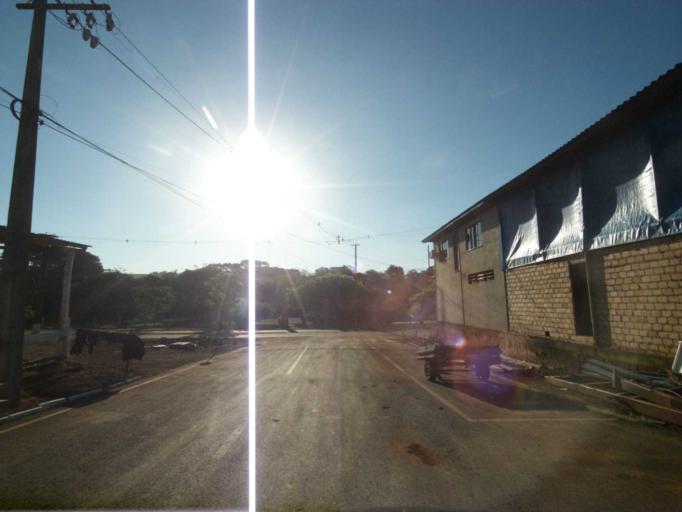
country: BR
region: Parana
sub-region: Coronel Vivida
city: Coronel Vivida
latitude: -25.9778
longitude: -52.8146
